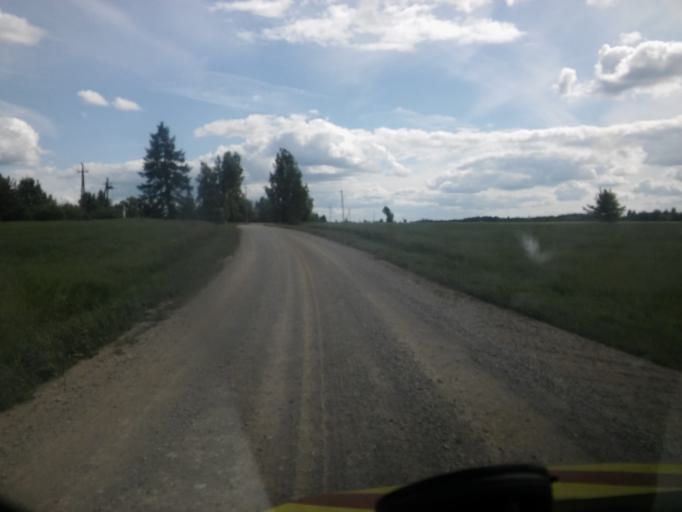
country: EE
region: Viljandimaa
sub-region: Karksi vald
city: Karksi-Nuia
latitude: 58.0757
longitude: 25.5198
